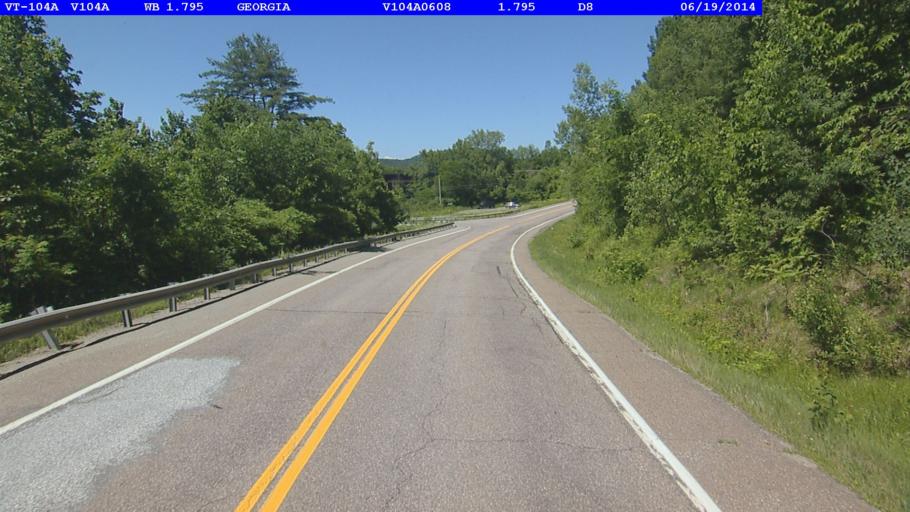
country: US
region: Vermont
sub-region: Chittenden County
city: Milton
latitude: 44.6804
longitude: -73.0808
